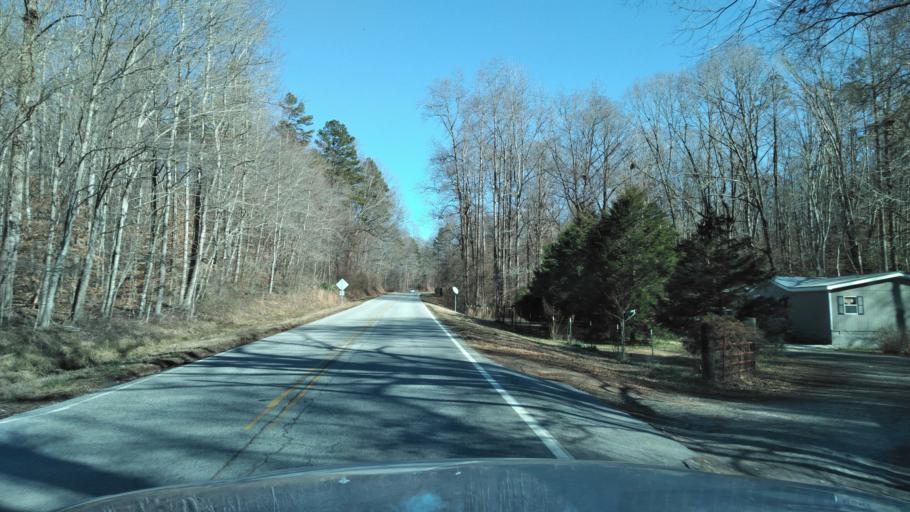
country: US
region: Georgia
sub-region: Hall County
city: Lula
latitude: 34.3180
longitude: -83.6868
